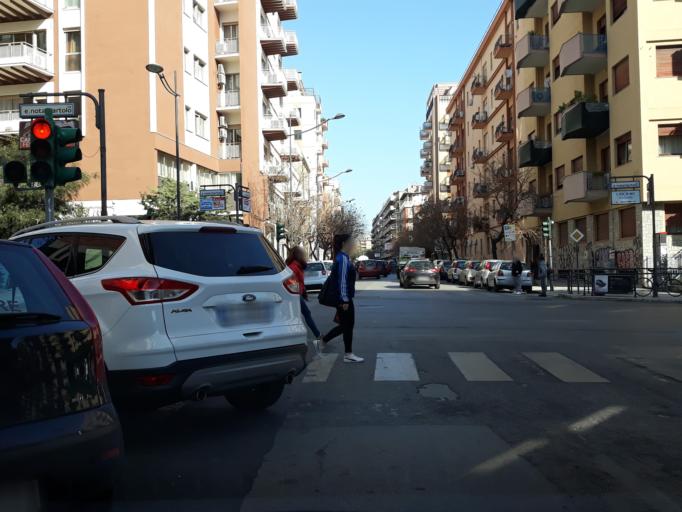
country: IT
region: Sicily
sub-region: Palermo
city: Palermo
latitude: 38.1327
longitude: 13.3467
